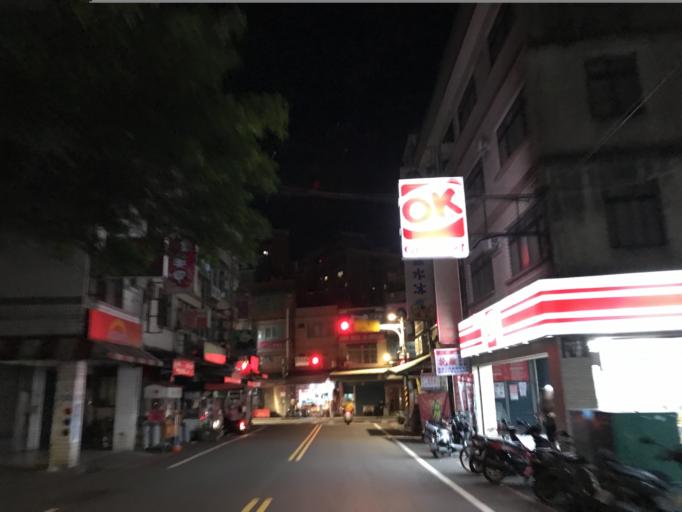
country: TW
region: Taiwan
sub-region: Taoyuan
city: Taoyuan
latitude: 24.9343
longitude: 121.3694
